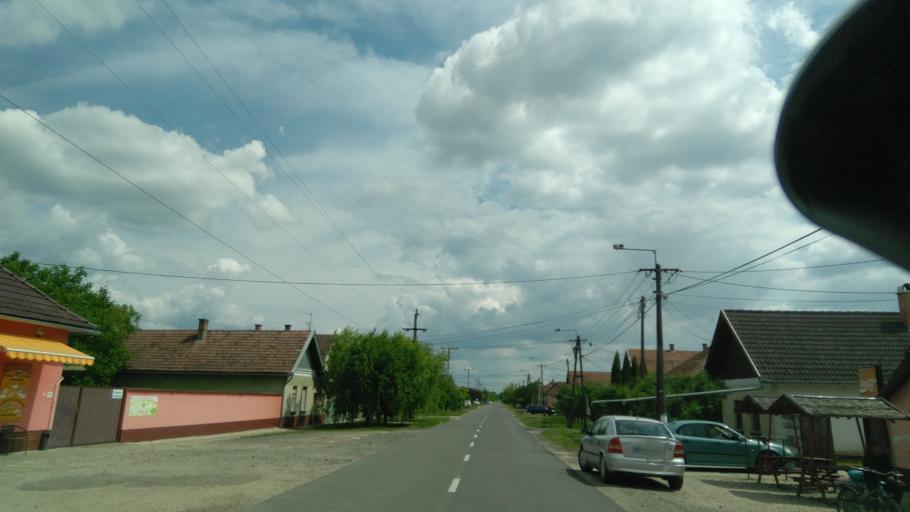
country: HU
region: Bekes
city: Totkomlos
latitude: 46.4071
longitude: 20.7444
